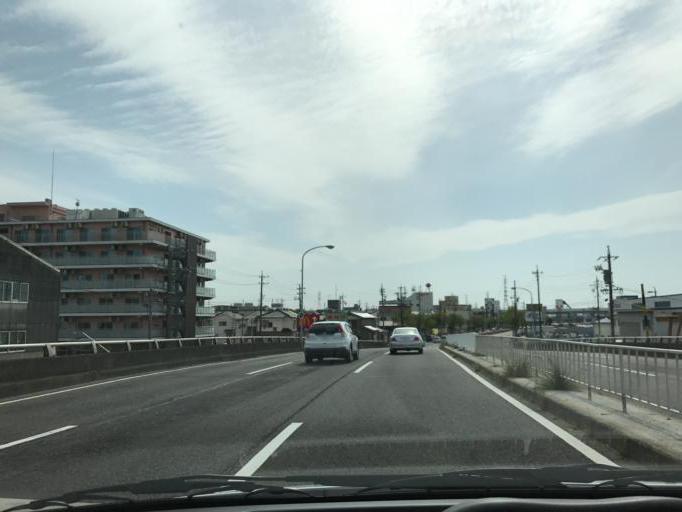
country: JP
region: Aichi
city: Obu
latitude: 35.0701
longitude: 136.9342
